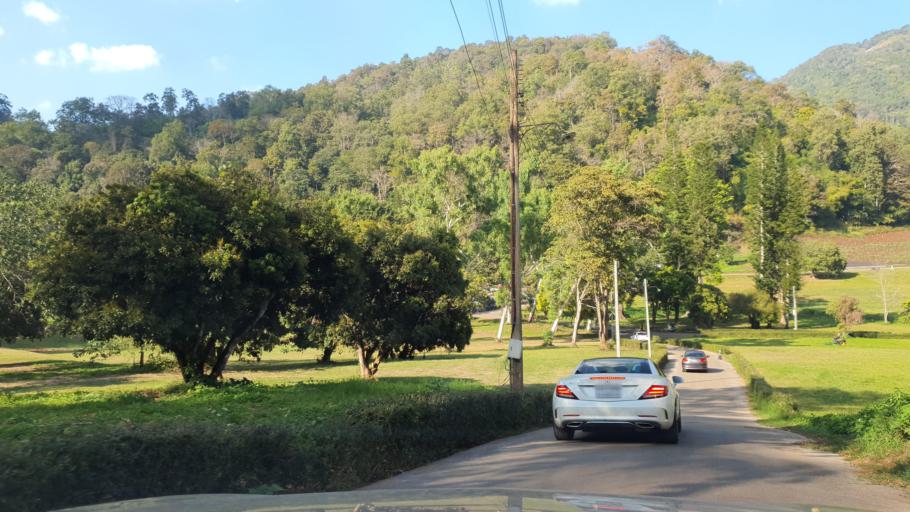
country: TH
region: Chiang Mai
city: Samoeng
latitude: 18.9012
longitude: 98.8230
